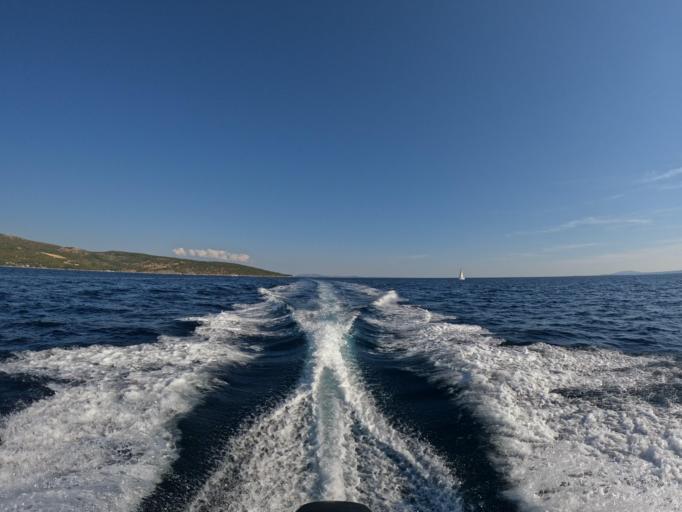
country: HR
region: Primorsko-Goranska
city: Punat
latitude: 44.9974
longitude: 14.6004
